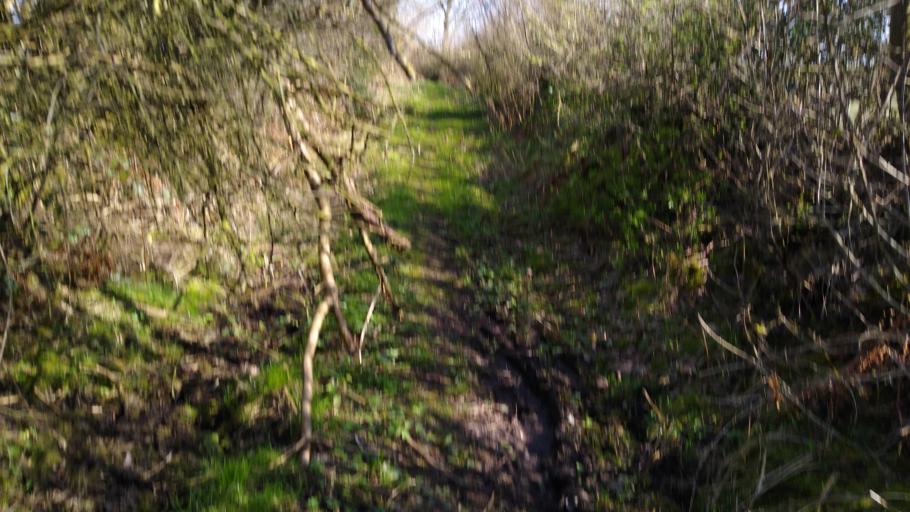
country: GB
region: England
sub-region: Cumbria
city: Dearham
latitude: 54.6755
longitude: -3.4250
